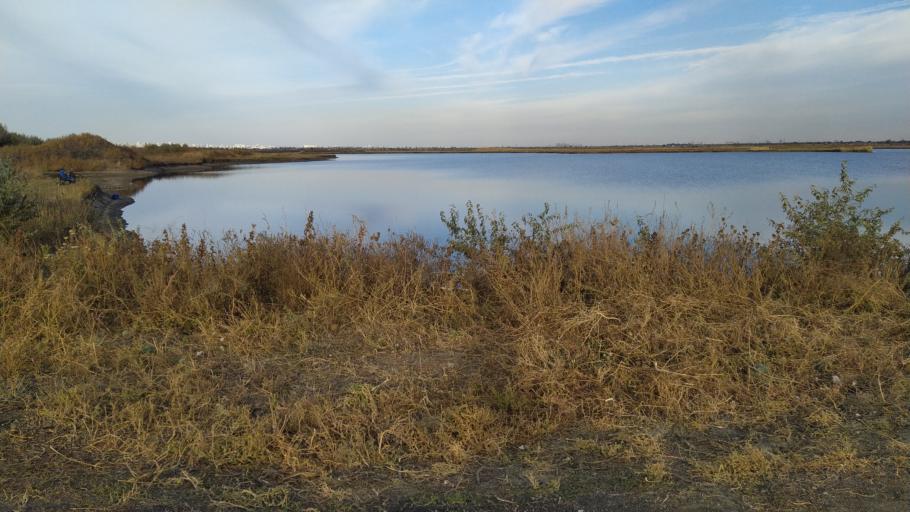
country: RU
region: Rostov
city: Kuleshovka
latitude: 47.1213
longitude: 39.6295
